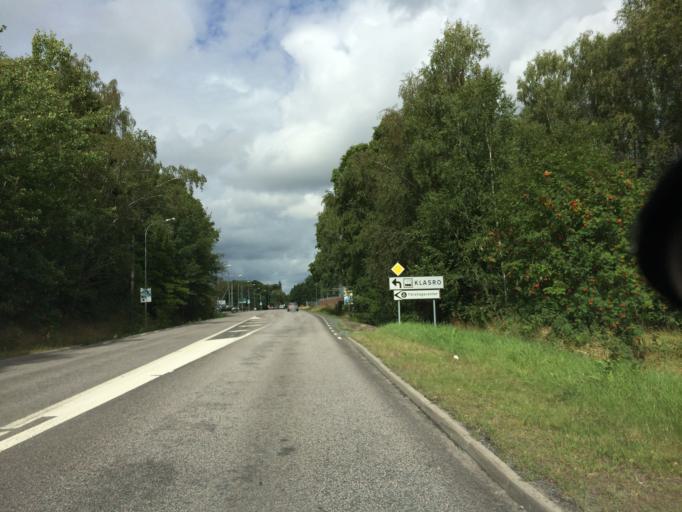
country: SE
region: Stockholm
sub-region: Sollentuna Kommun
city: Sollentuna
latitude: 59.4459
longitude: 17.9258
